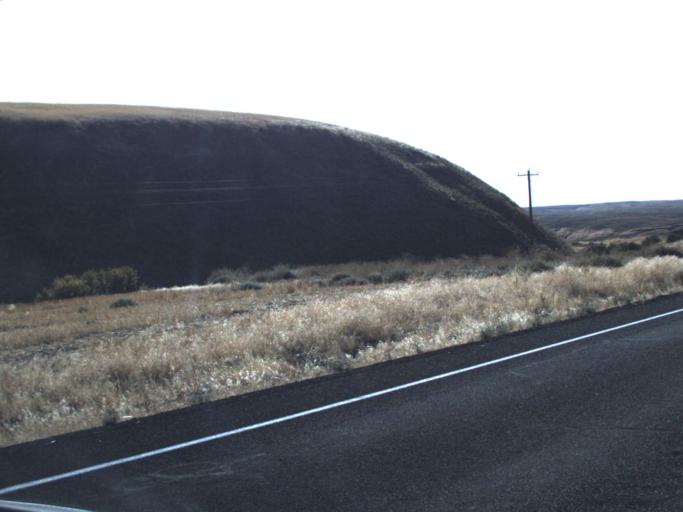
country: US
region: Washington
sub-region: Walla Walla County
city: Garrett
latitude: 46.2908
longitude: -118.5237
